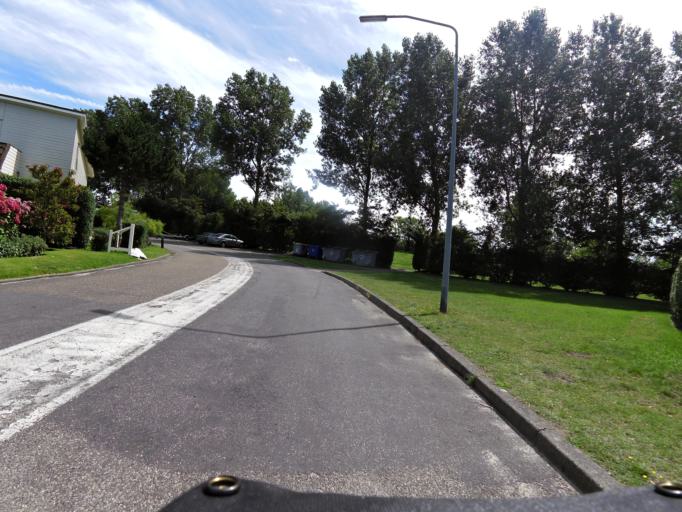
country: NL
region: Zeeland
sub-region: Gemeente Noord-Beveland
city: Kamperland
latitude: 51.5904
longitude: 3.7157
